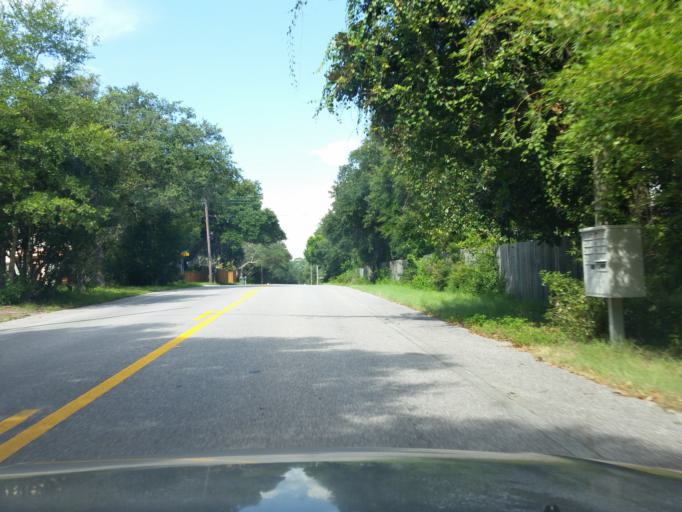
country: US
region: Alabama
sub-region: Baldwin County
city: Orange Beach
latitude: 30.3141
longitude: -87.4512
